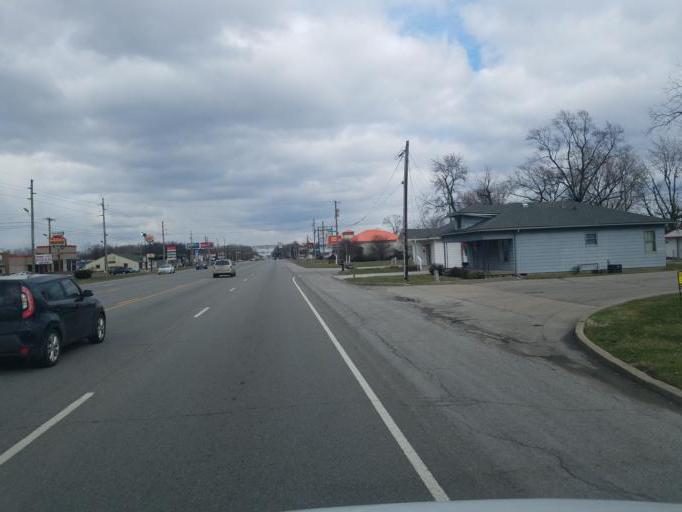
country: US
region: Indiana
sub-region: Marion County
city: Speedway
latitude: 39.7641
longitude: -86.2933
